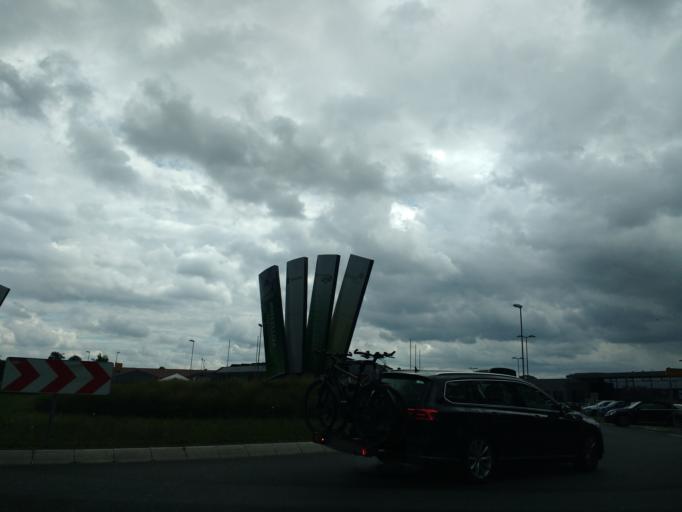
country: DE
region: Lower Saxony
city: Glandorf
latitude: 52.0796
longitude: 8.0008
